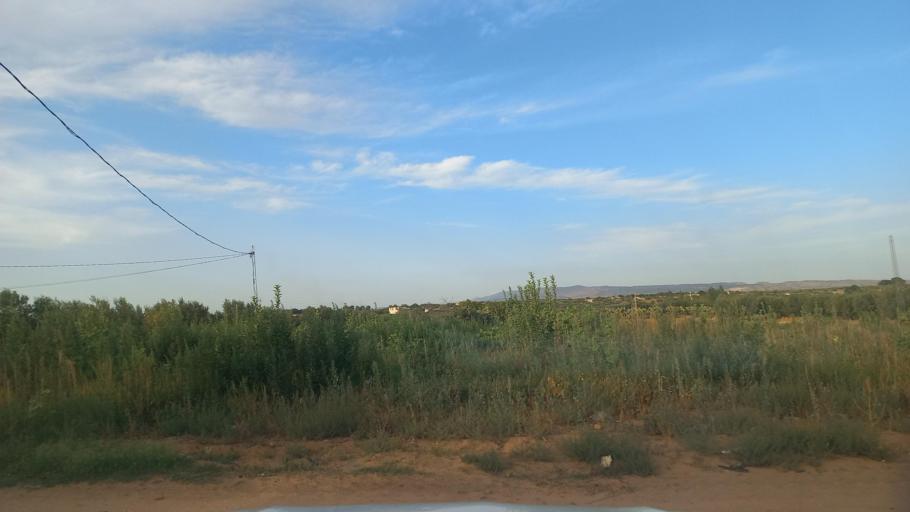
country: TN
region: Al Qasrayn
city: Kasserine
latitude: 35.2512
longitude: 9.0394
